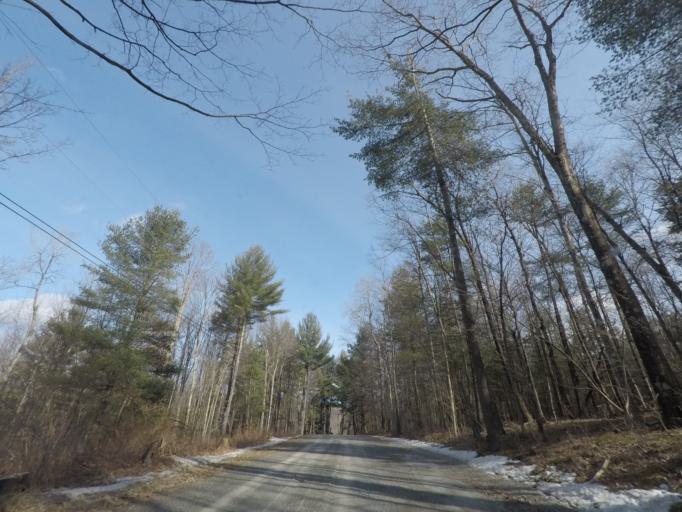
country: US
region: New York
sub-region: Rensselaer County
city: Nassau
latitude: 42.5599
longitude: -73.5677
